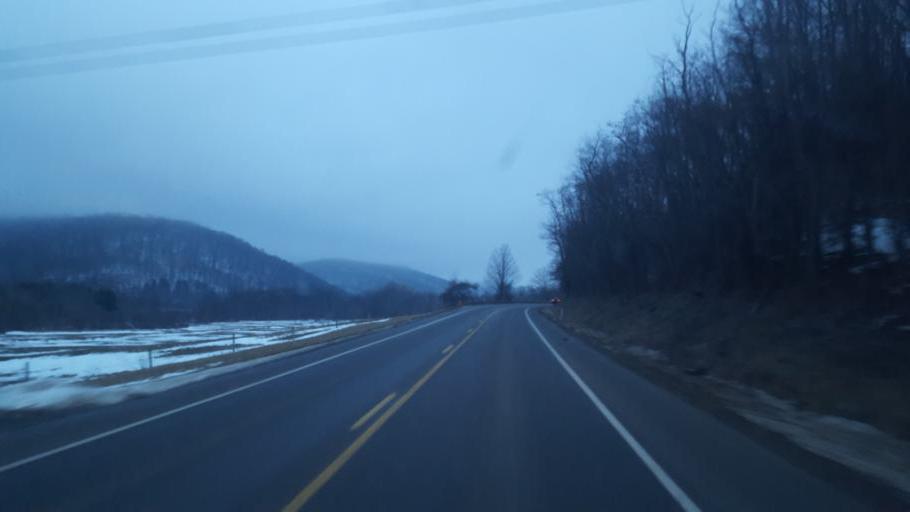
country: US
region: Pennsylvania
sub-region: Potter County
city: Coudersport
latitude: 41.7444
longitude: -78.0876
